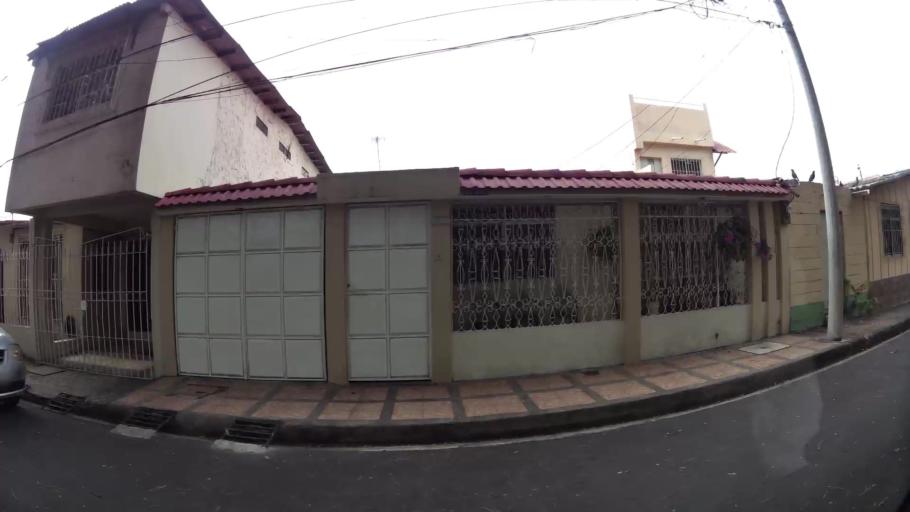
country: EC
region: Guayas
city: Eloy Alfaro
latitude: -2.1372
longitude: -79.8968
